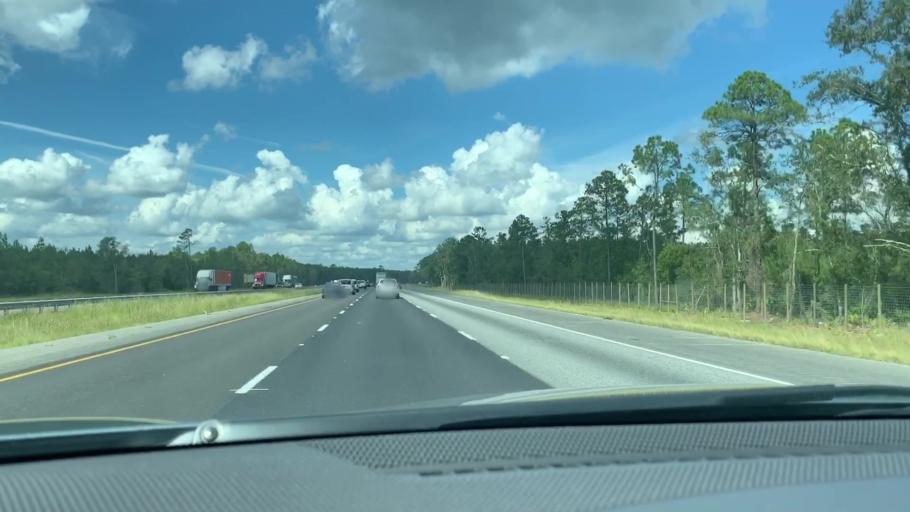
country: US
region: Georgia
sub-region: Camden County
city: Kingsland
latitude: 30.8655
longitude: -81.6810
